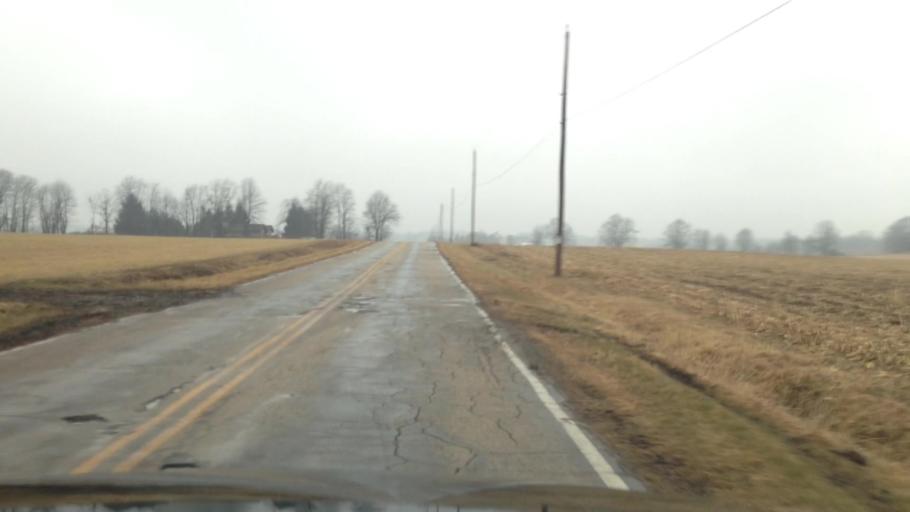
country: US
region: Wisconsin
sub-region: Washington County
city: Richfield
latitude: 43.2576
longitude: -88.1647
